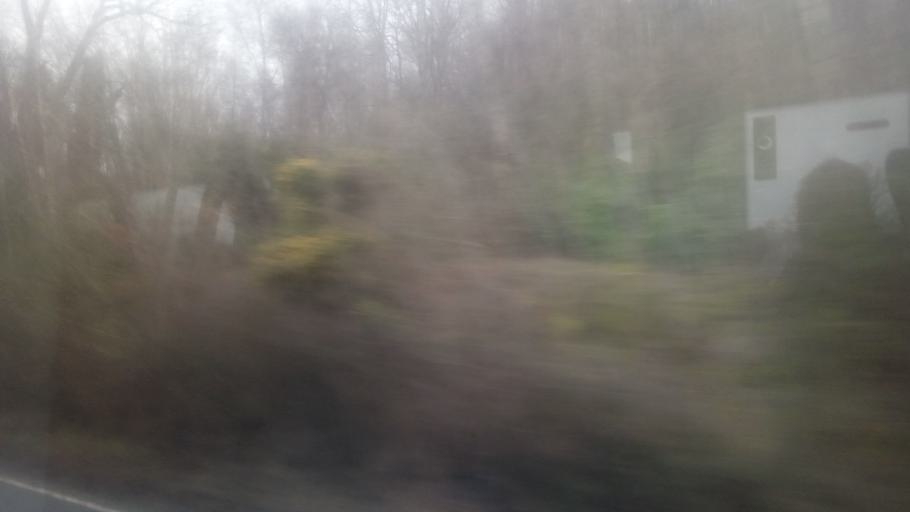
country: GB
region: Scotland
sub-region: The Scottish Borders
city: Jedburgh
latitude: 55.5218
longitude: -2.5885
